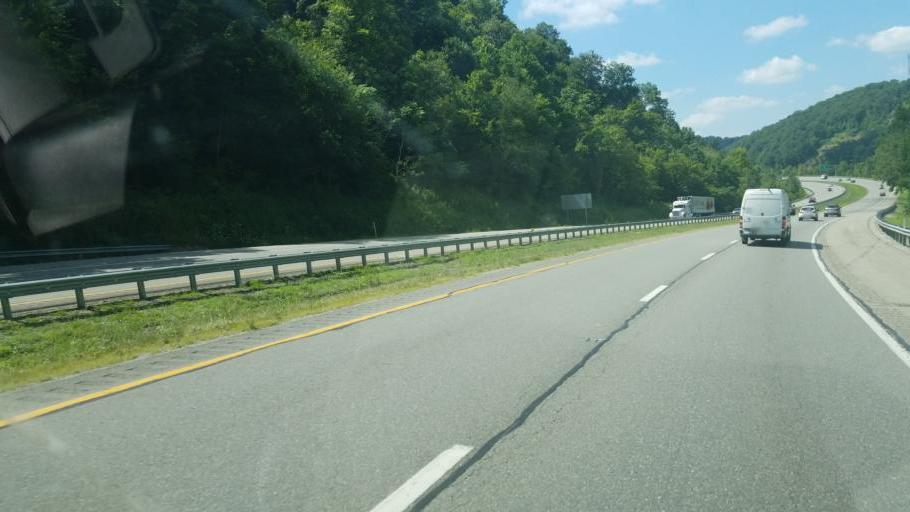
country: US
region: West Virginia
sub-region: Kanawha County
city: Charleston
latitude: 38.4057
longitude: -81.6226
